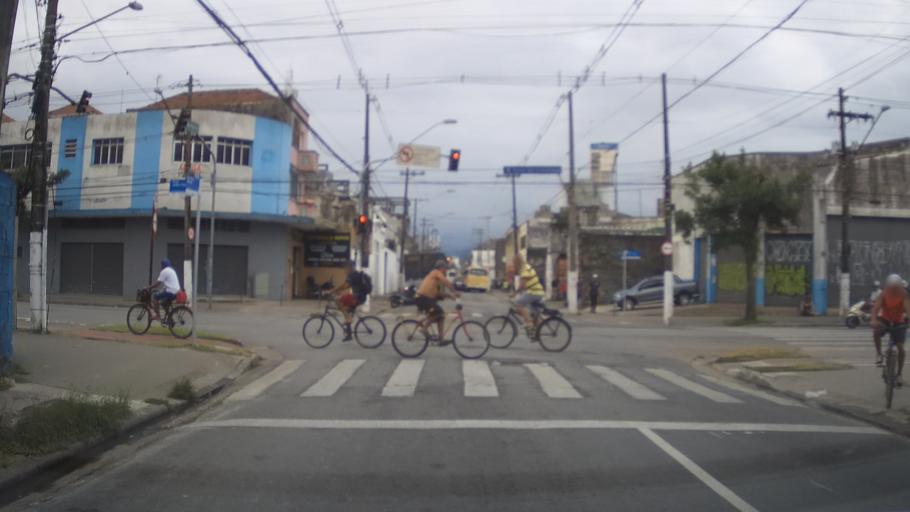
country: BR
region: Sao Paulo
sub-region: Santos
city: Santos
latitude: -23.9364
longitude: -46.3208
